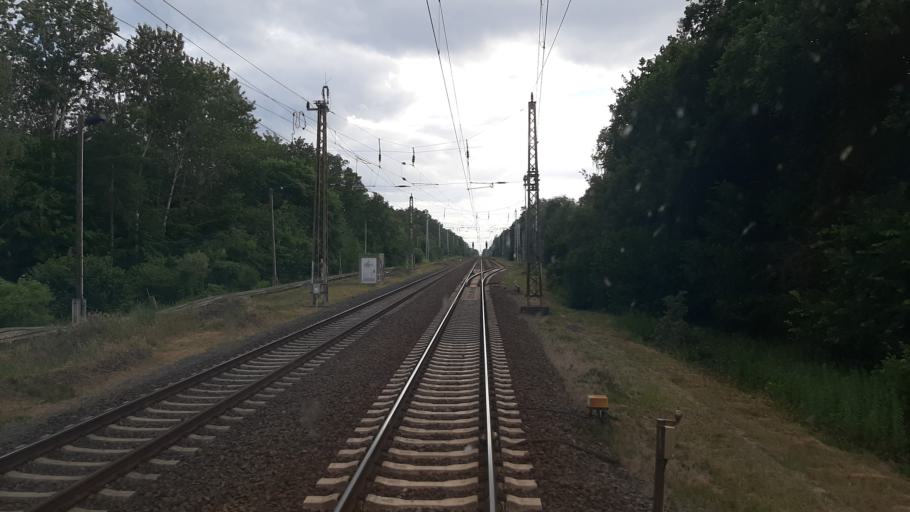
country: DE
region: Brandenburg
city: Brieselang
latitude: 52.5910
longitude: 13.0433
